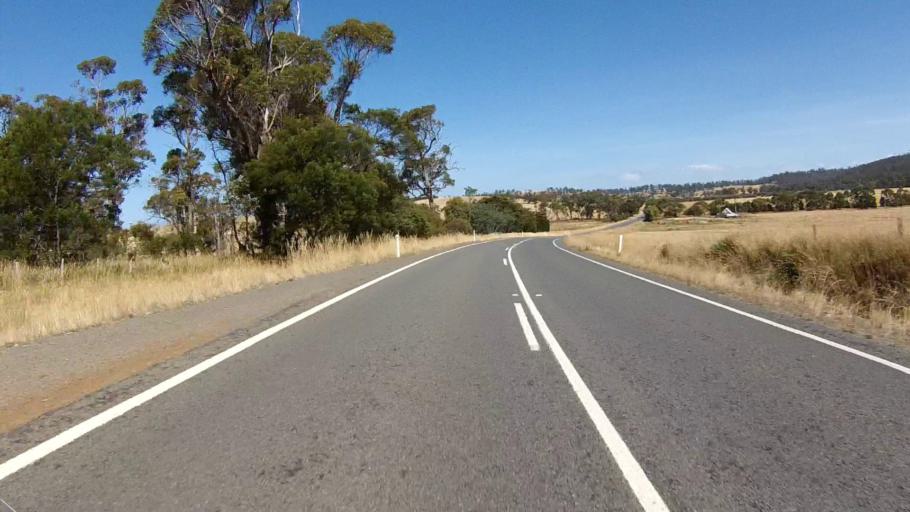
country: AU
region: Tasmania
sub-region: Sorell
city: Sorell
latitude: -42.4524
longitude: 147.9302
